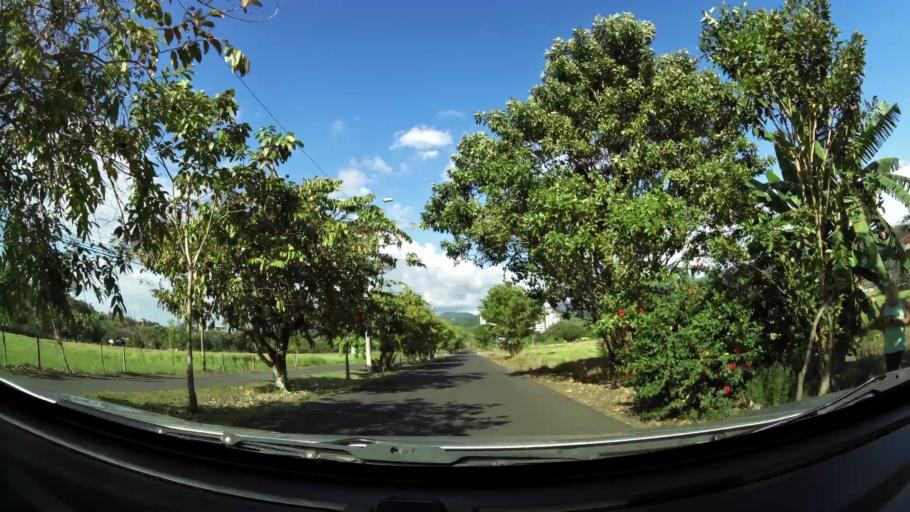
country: CR
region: Puntarenas
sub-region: Canton de Garabito
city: Jaco
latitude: 9.6289
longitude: -84.6321
